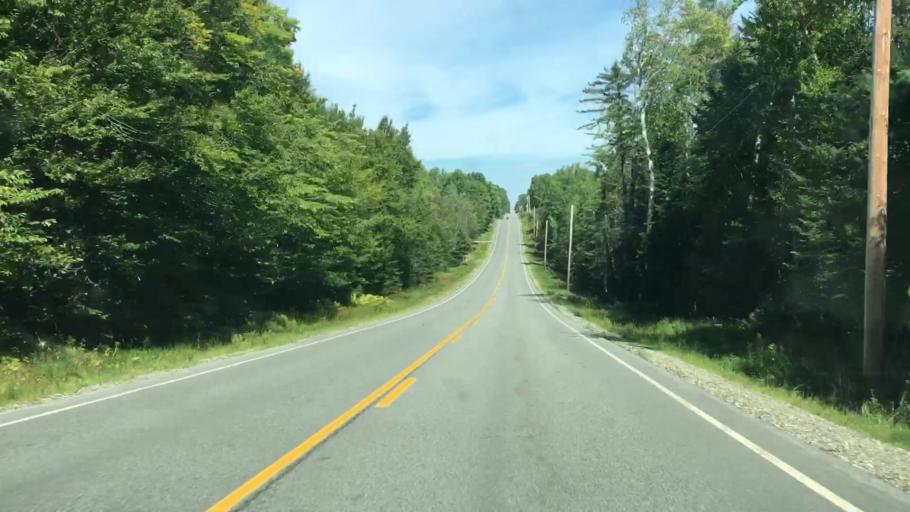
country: US
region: Maine
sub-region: Penobscot County
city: Howland
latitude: 45.2094
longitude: -68.8023
